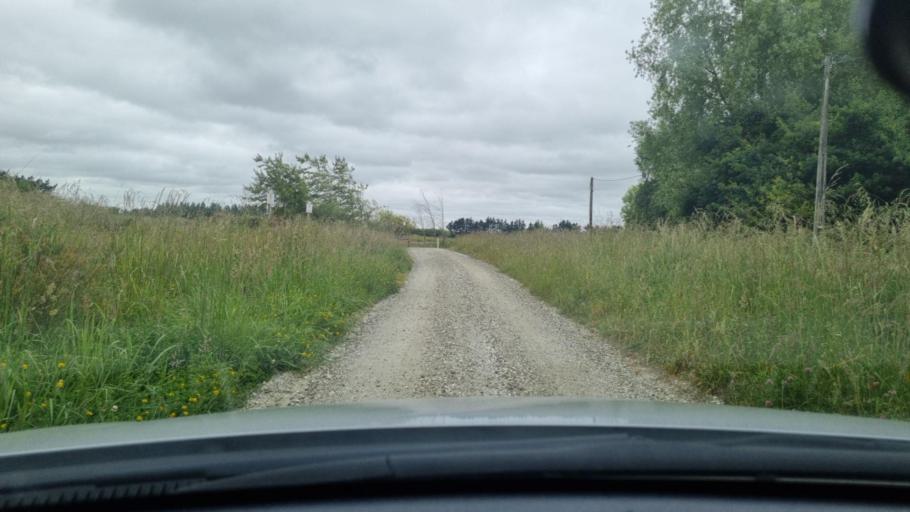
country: NZ
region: Southland
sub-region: Invercargill City
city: Invercargill
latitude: -46.3492
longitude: 168.3401
